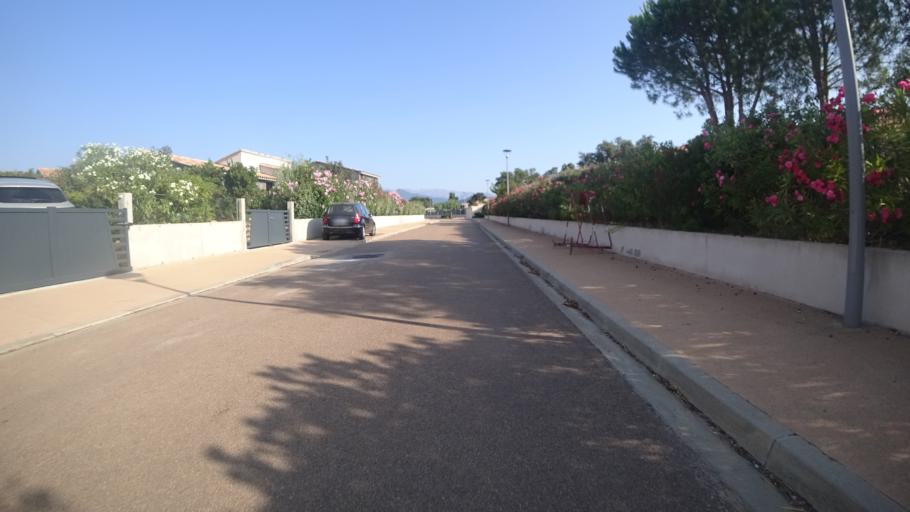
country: FR
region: Corsica
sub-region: Departement de la Corse-du-Sud
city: Porto-Vecchio
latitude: 41.6385
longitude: 9.3392
